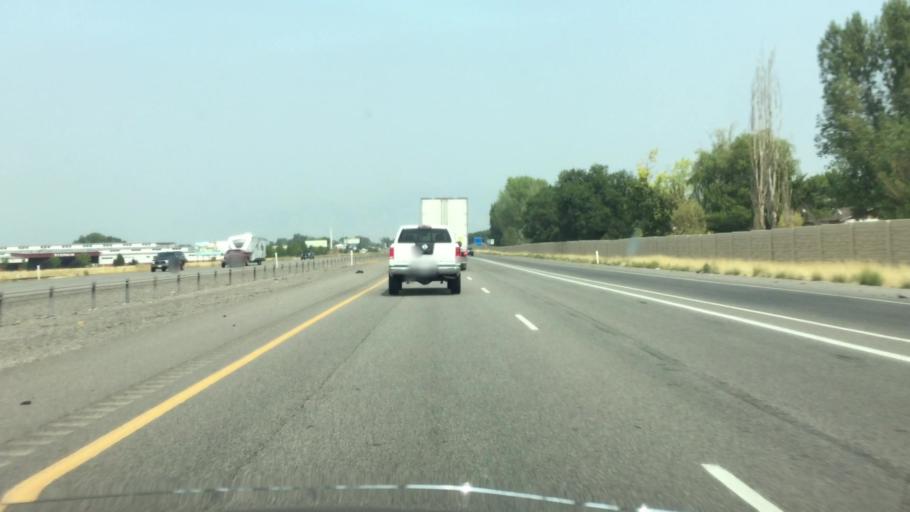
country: US
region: Utah
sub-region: Utah County
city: Payson
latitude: 40.0363
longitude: -111.7521
